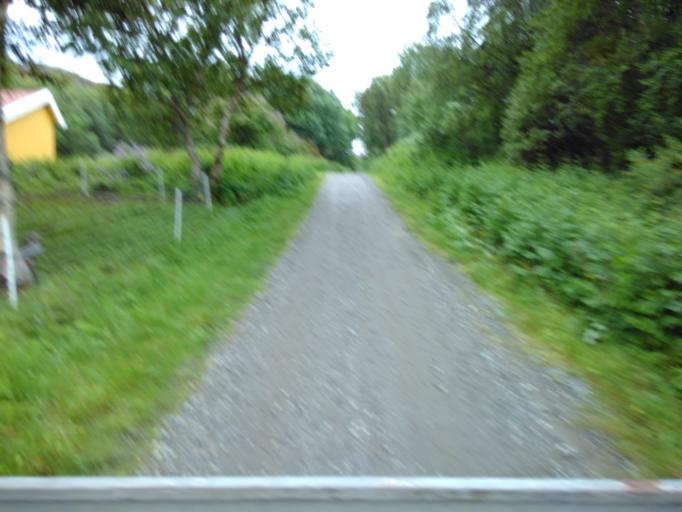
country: NO
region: Nordland
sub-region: Gildeskal
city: Inndyr
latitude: 67.2798
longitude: 14.0029
